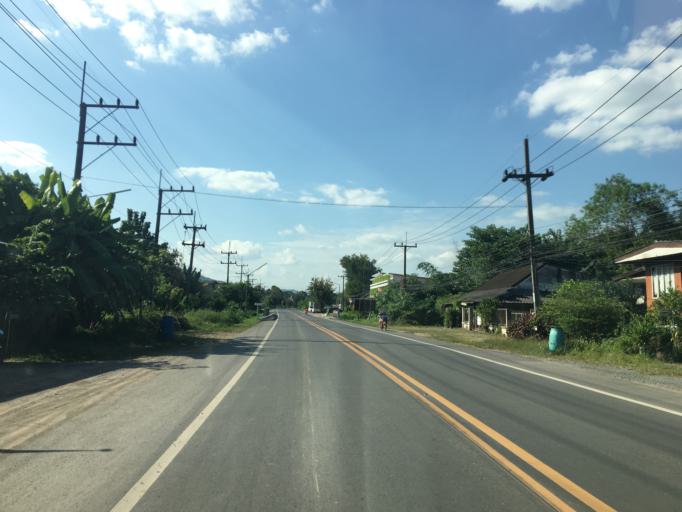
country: TH
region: Phayao
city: Chun
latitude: 19.3437
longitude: 100.1200
